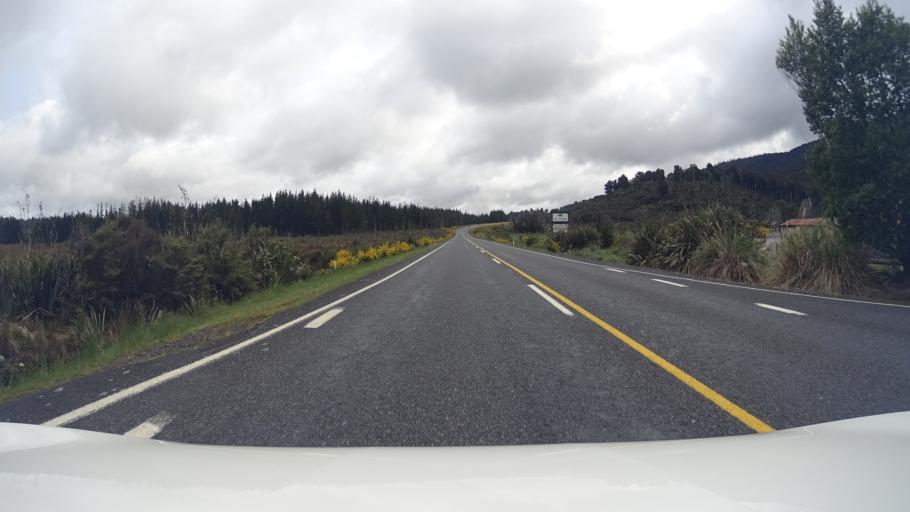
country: NZ
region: Manawatu-Wanganui
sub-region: Ruapehu District
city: Waiouru
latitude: -39.2272
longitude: 175.3960
